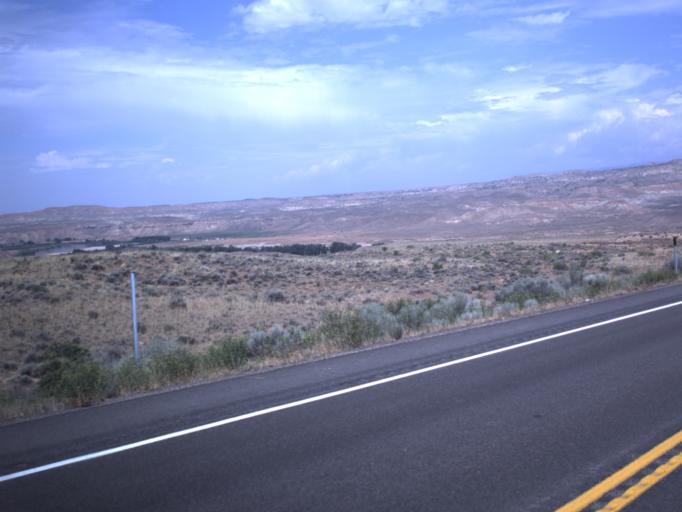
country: US
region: Utah
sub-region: Uintah County
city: Naples
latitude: 40.2934
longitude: -109.4765
